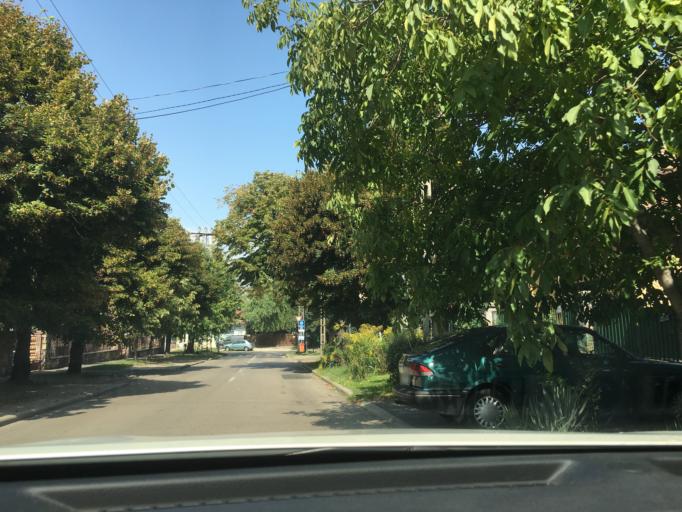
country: HU
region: Budapest
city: Budapest XVII. keruelet
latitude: 47.4822
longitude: 19.2746
